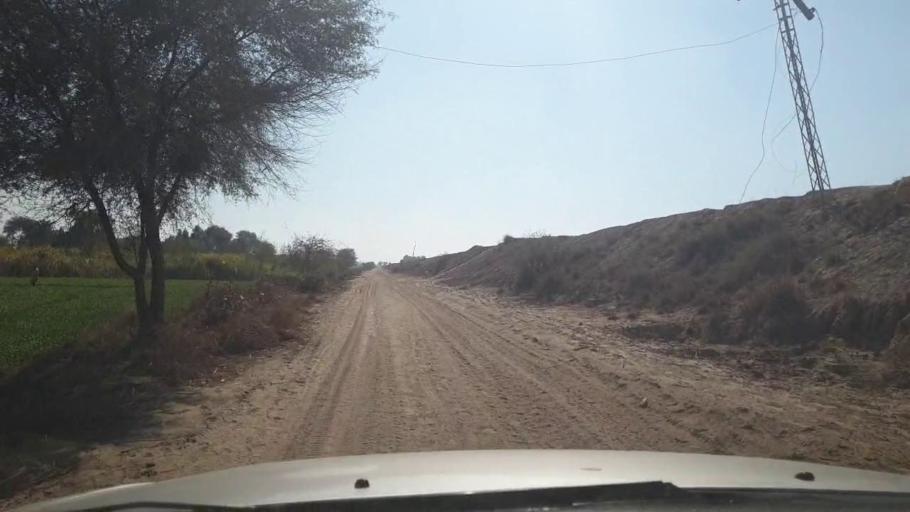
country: PK
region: Sindh
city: Ghotki
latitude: 28.0265
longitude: 69.2102
